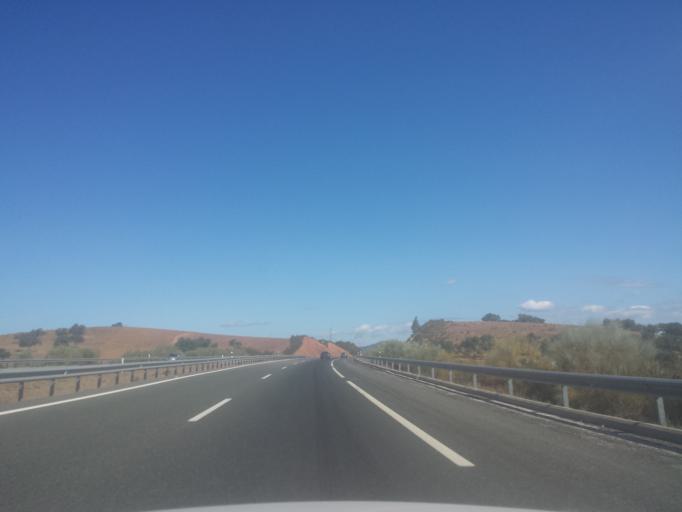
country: ES
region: Andalusia
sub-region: Provincia de Huelva
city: Santa Olalla del Cala
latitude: 37.8187
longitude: -6.2114
